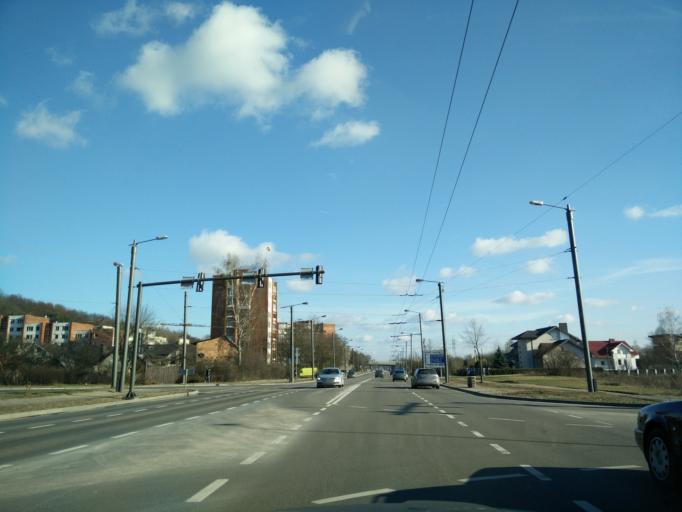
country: LT
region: Kauno apskritis
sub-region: Kauno rajonas
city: Akademija (Kaunas)
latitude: 54.9191
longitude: 23.8293
